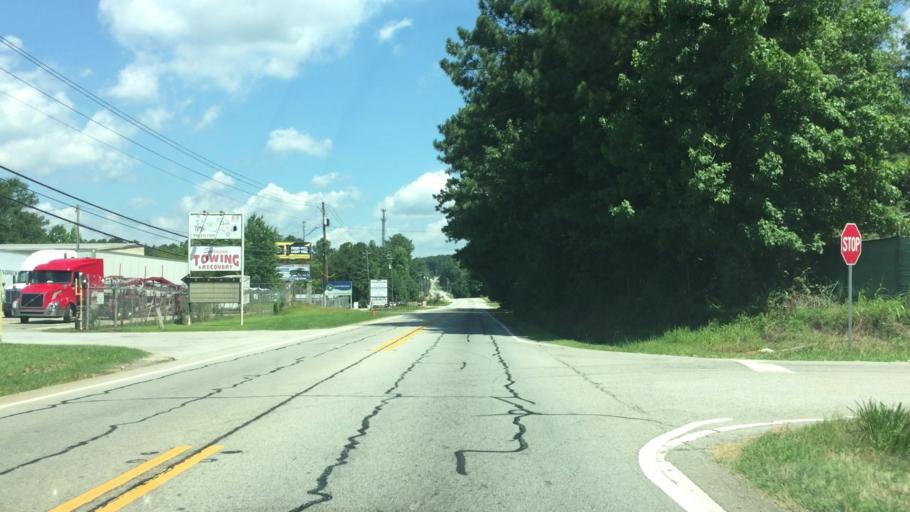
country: US
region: Georgia
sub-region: Henry County
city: Stockbridge
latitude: 33.5300
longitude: -84.1979
